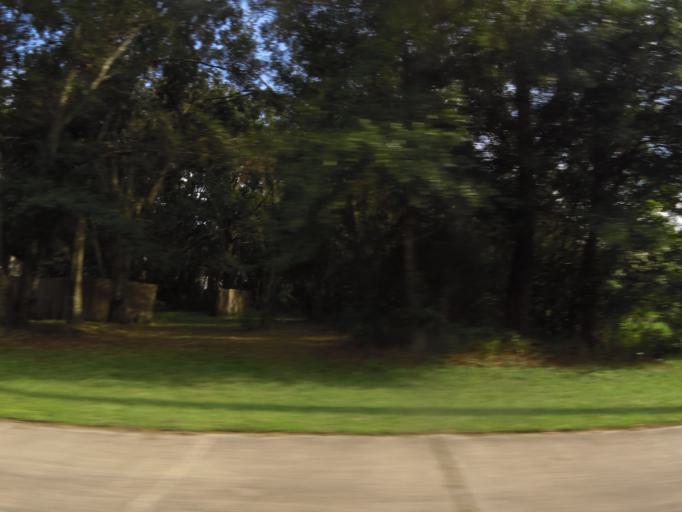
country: US
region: Florida
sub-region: Saint Johns County
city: Fruit Cove
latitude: 30.1840
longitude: -81.6045
